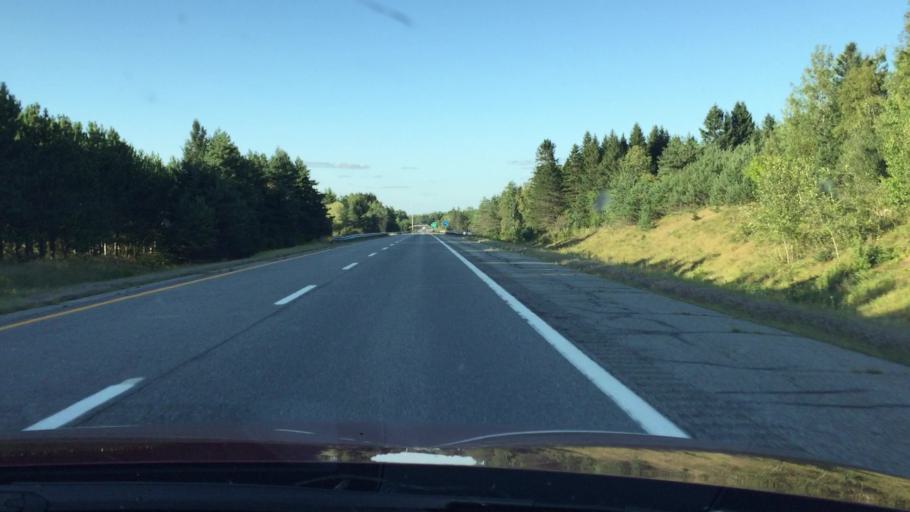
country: US
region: Maine
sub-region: Penobscot County
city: Patten
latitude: 45.8623
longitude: -68.4193
